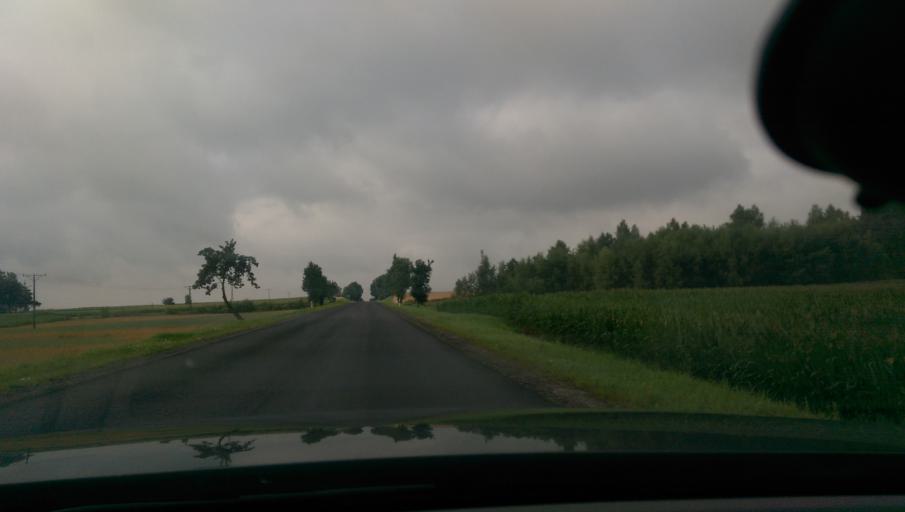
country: PL
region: Masovian Voivodeship
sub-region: Powiat przasnyski
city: Przasnysz
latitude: 53.0896
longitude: 20.8547
